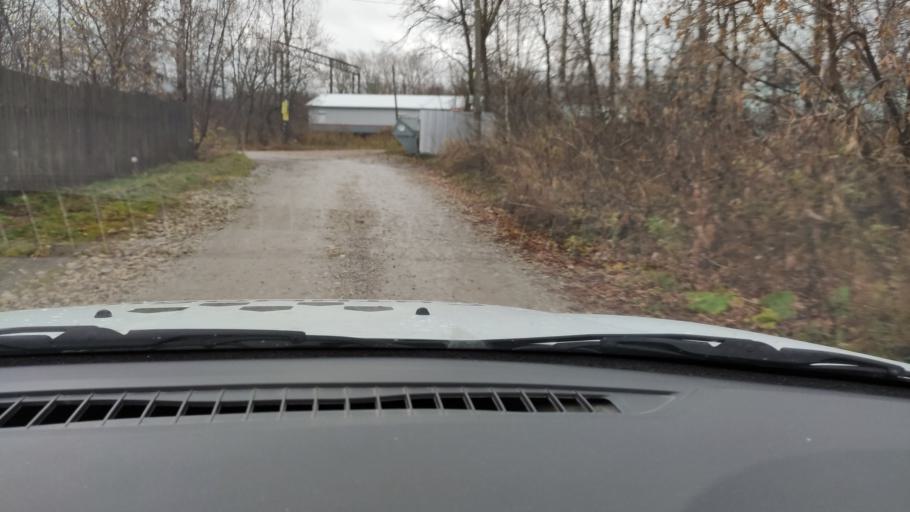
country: RU
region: Perm
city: Sylva
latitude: 58.0455
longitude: 56.7379
